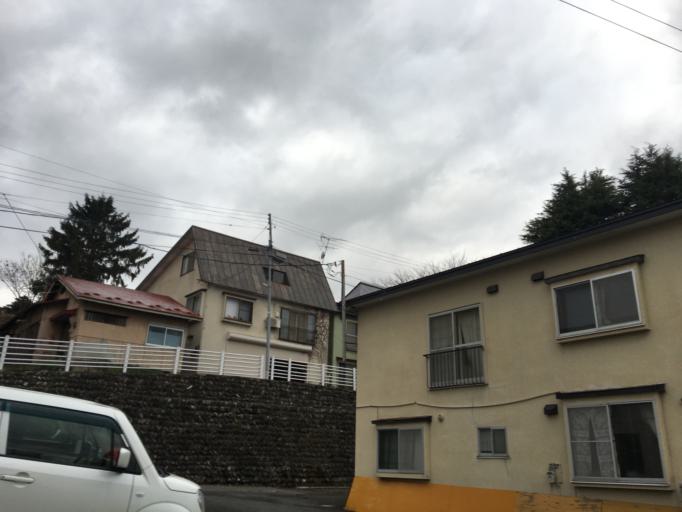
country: JP
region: Aomori
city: Hirosaki
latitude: 40.5936
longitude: 140.4676
